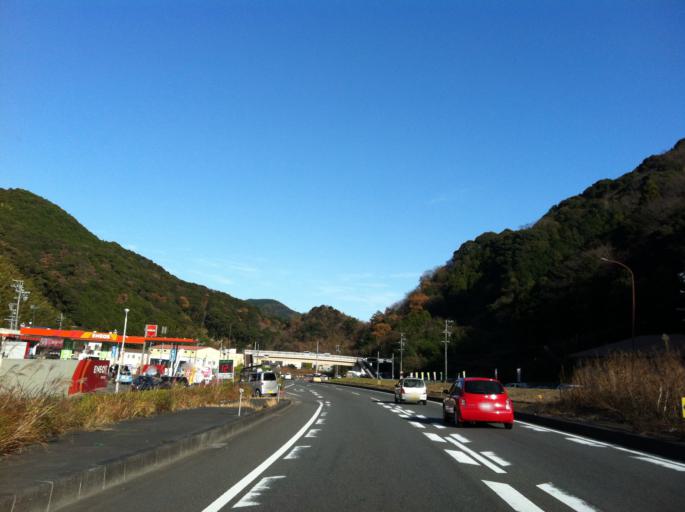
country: JP
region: Shizuoka
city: Yaizu
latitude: 34.9393
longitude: 138.3180
